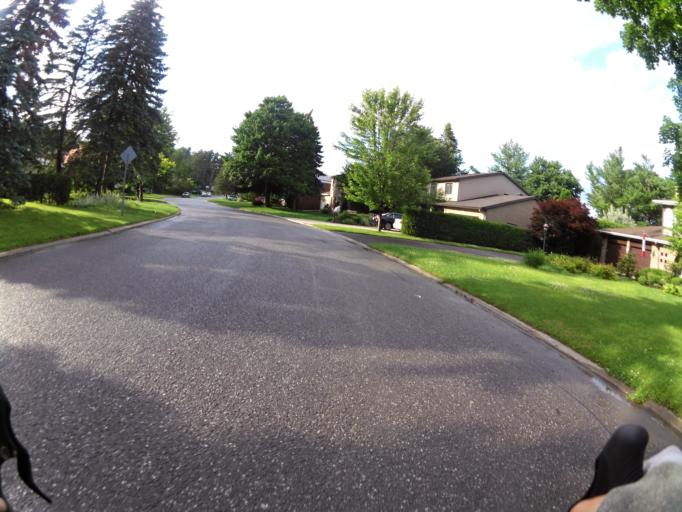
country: CA
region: Ontario
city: Bells Corners
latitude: 45.3223
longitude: -75.7844
